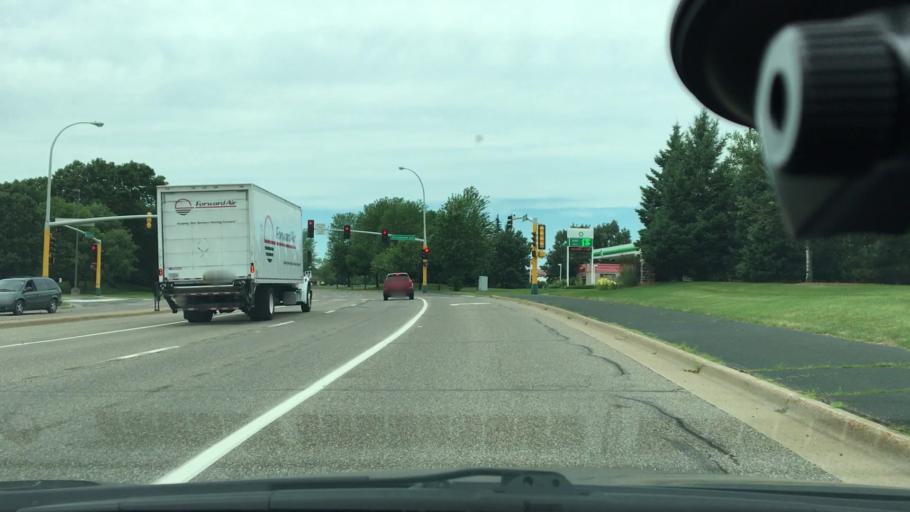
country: US
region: Minnesota
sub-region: Hennepin County
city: Maple Grove
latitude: 45.0640
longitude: -93.4399
